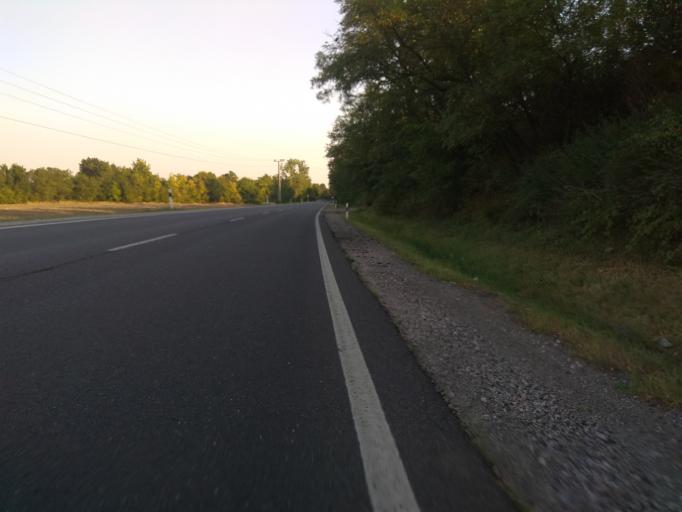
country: HU
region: Borsod-Abauj-Zemplen
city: Nyekladhaza
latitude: 47.9627
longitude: 20.8339
